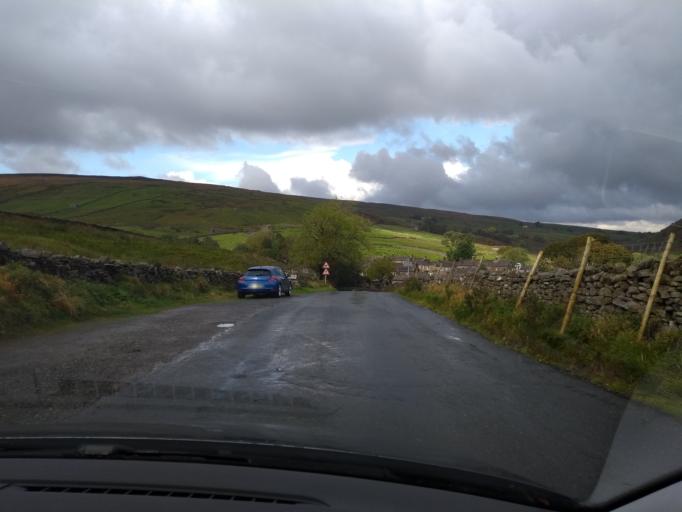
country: GB
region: England
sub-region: County Durham
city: Bowes
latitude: 54.3777
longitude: -2.1666
